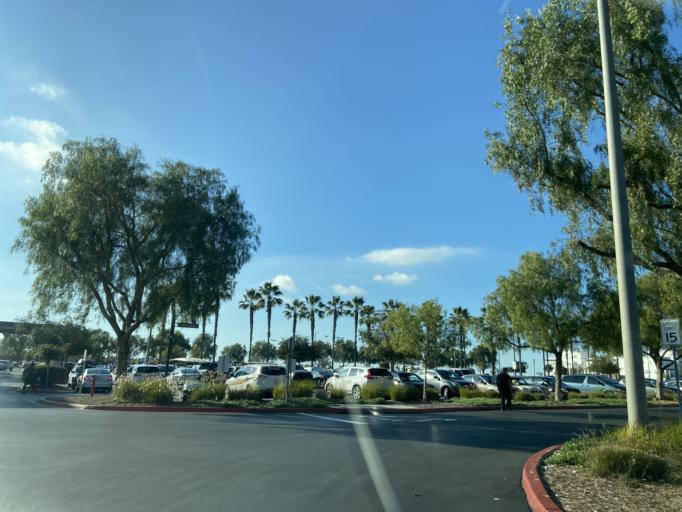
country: US
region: California
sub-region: San Diego County
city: Bonita
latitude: 32.6246
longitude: -116.9670
